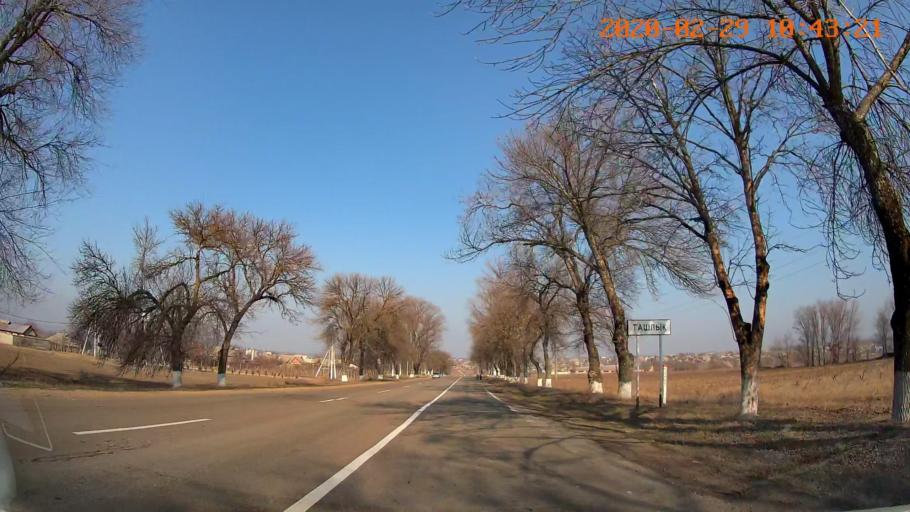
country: MD
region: Telenesti
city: Grigoriopol
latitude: 47.0603
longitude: 29.4039
